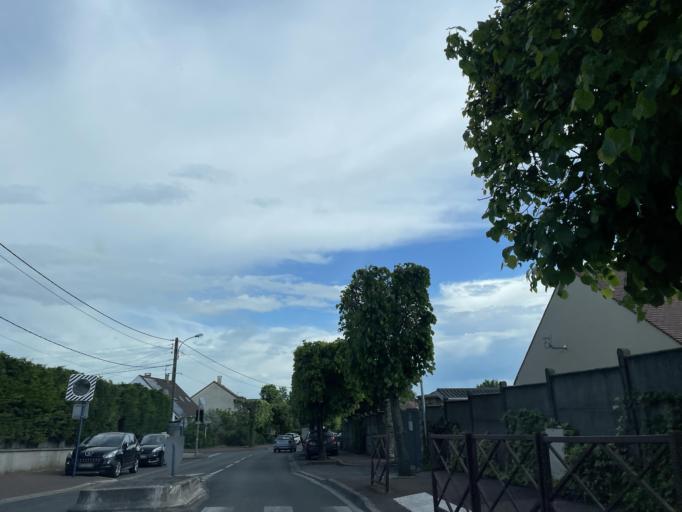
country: FR
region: Ile-de-France
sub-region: Departement du Val-d'Oise
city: Arnouville
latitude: 48.9826
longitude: 2.4211
